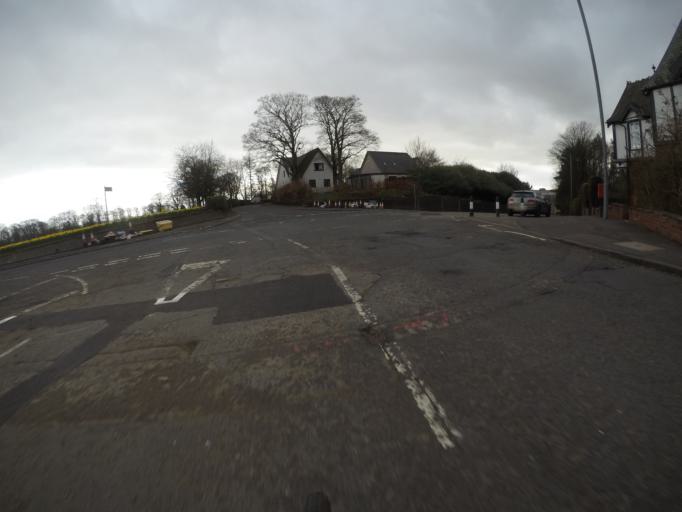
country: GB
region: Scotland
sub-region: East Ayrshire
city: Kilmarnock
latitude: 55.6154
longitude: -4.4876
